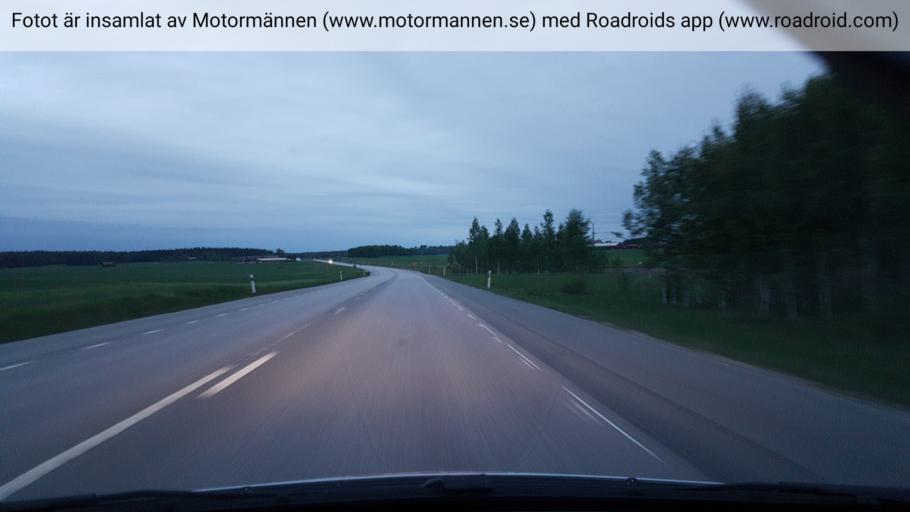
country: SE
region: Vaestmanland
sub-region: Sala Kommun
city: Sala
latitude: 59.9281
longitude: 16.6976
